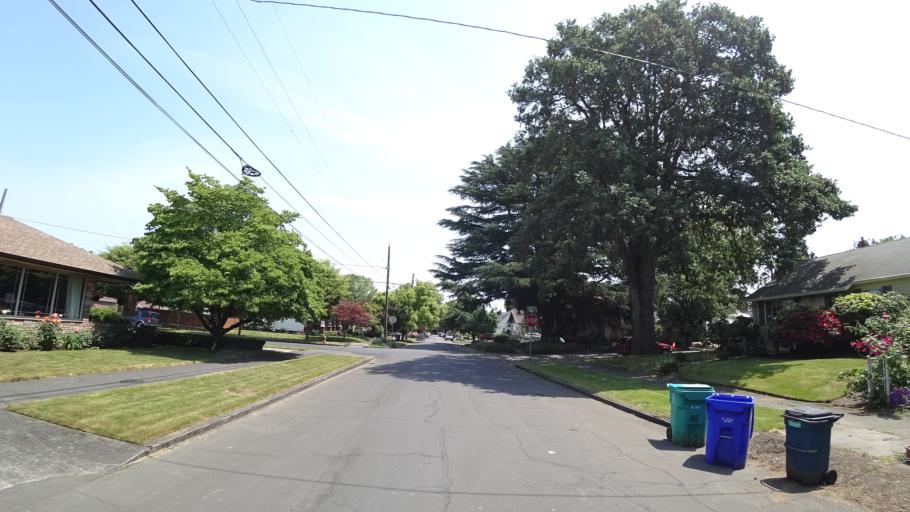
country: US
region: Oregon
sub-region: Multnomah County
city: Portland
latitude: 45.5810
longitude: -122.6851
